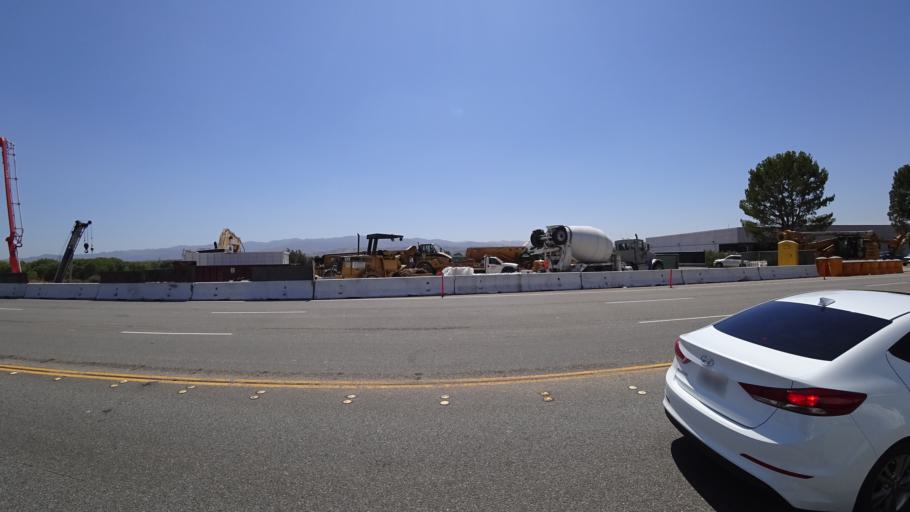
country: US
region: California
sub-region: Los Angeles County
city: Santa Clarita
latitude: 34.4352
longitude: -118.5622
